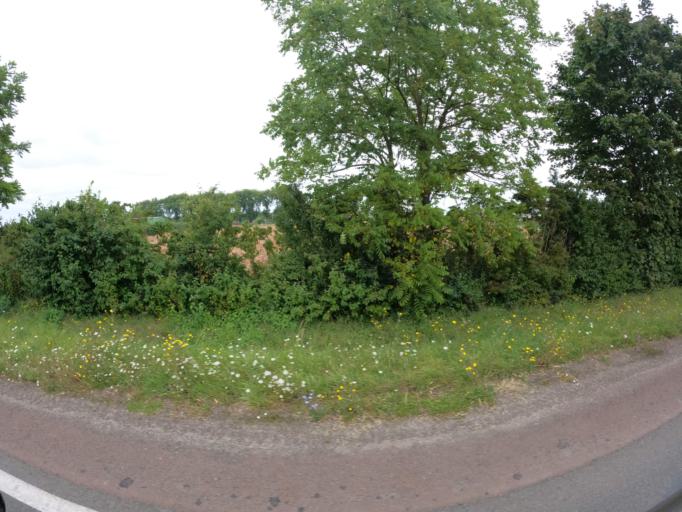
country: FR
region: Pays de la Loire
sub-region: Departement de la Vendee
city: Saint-Hilaire-des-Loges
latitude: 46.4075
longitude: -0.6810
